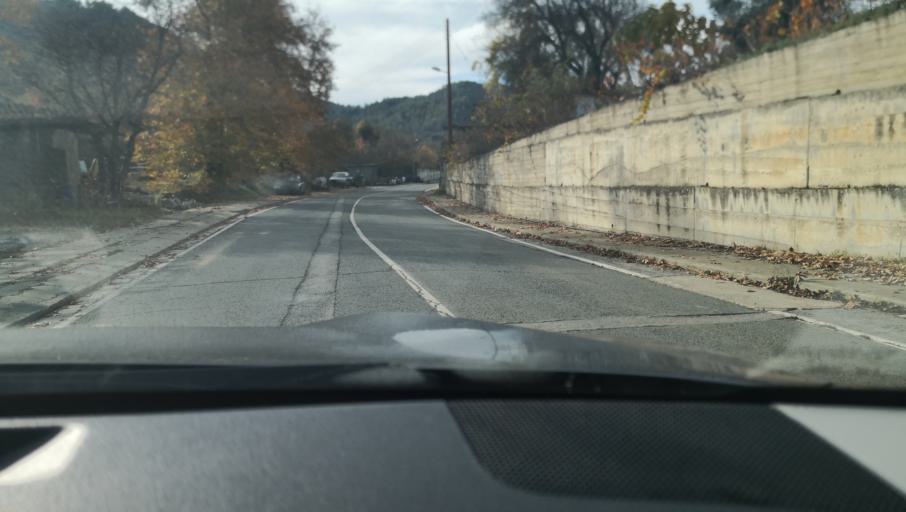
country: CY
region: Lefkosia
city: Lefka
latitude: 35.0315
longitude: 32.7301
